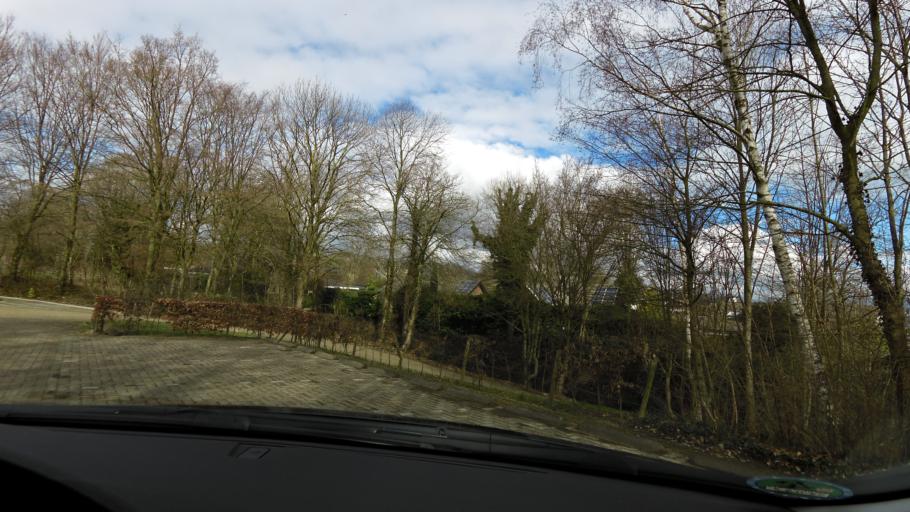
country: NL
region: Limburg
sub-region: Gemeente Nuth
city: Nuth
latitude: 50.9049
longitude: 5.8795
